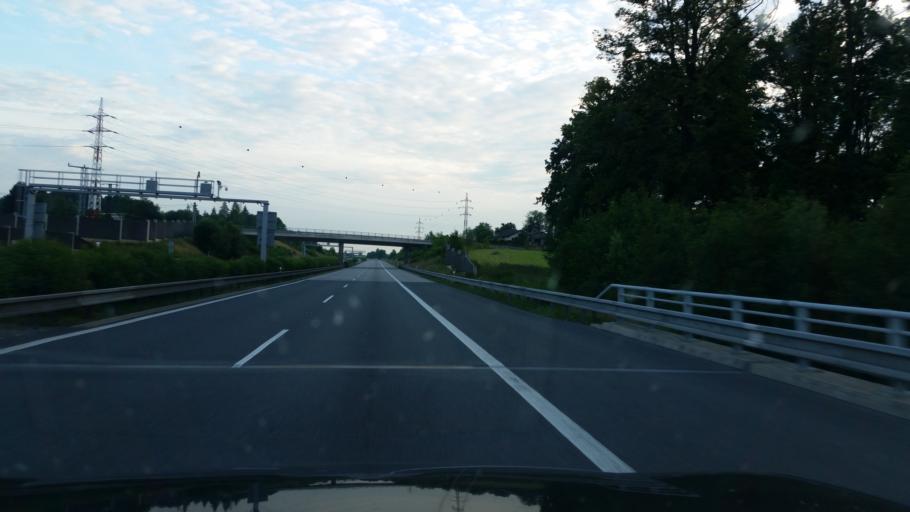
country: CZ
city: Klimkovice
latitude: 49.7871
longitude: 18.1078
